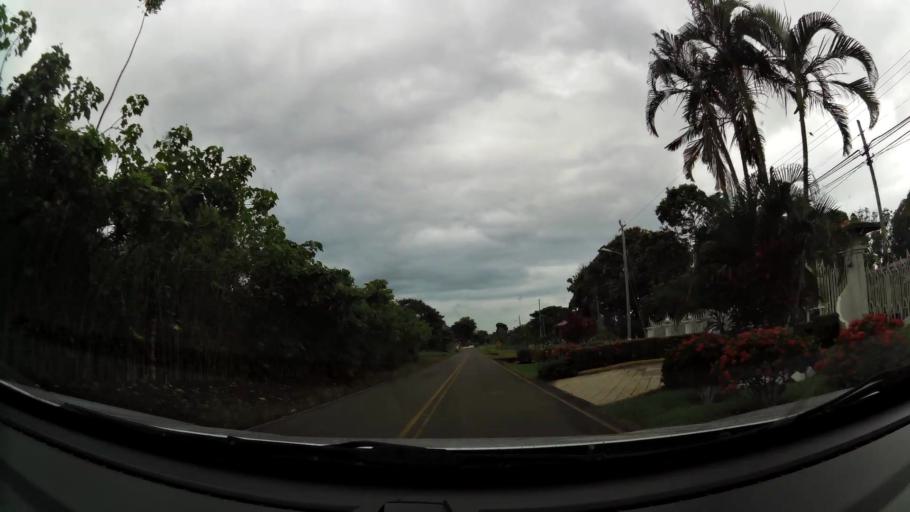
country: CR
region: Puntarenas
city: Esparza
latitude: 9.9681
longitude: -84.6153
